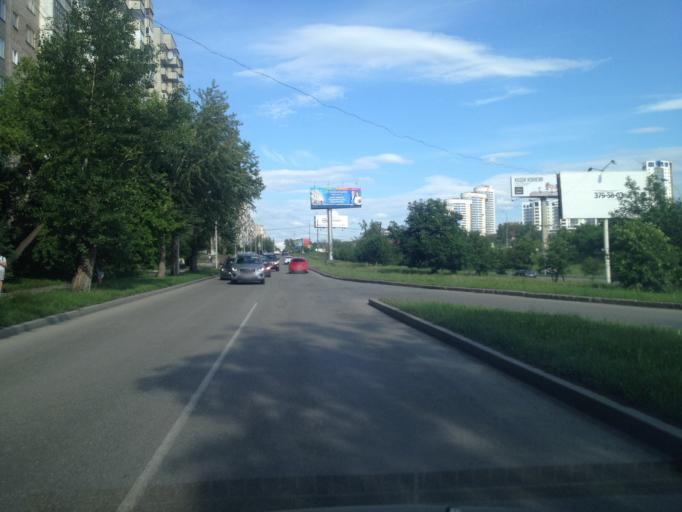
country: RU
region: Sverdlovsk
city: Shirokaya Rechka
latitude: 56.8270
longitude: 60.5399
